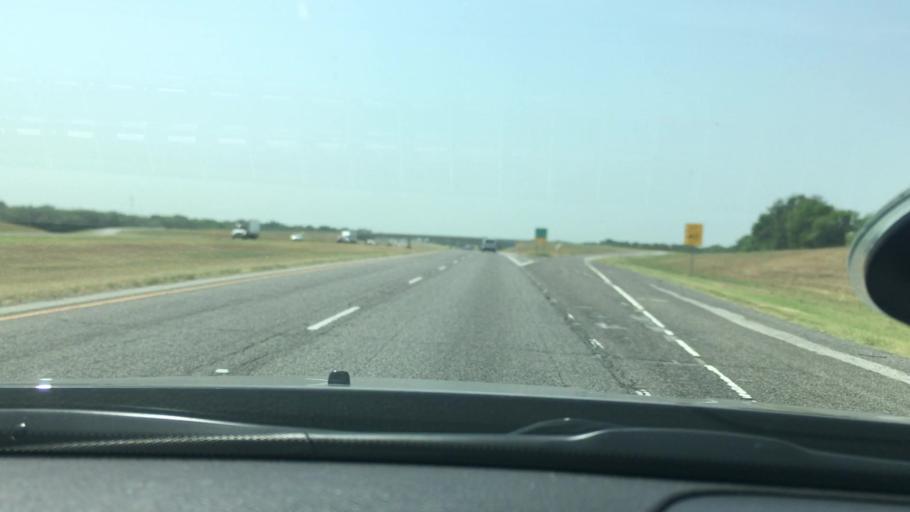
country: US
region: Oklahoma
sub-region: Garvin County
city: Wynnewood
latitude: 34.5761
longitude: -97.2009
